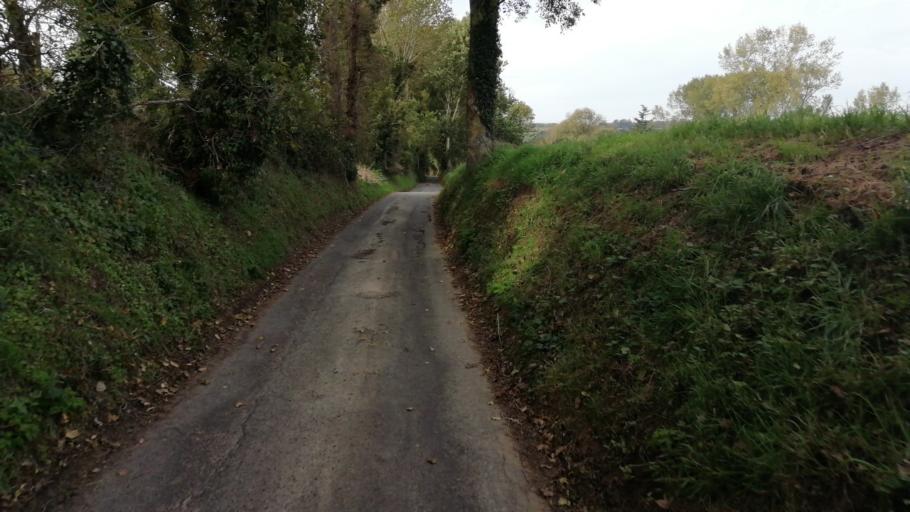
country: FR
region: Haute-Normandie
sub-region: Departement de la Seine-Maritime
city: Epouville
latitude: 49.5445
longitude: 0.2114
